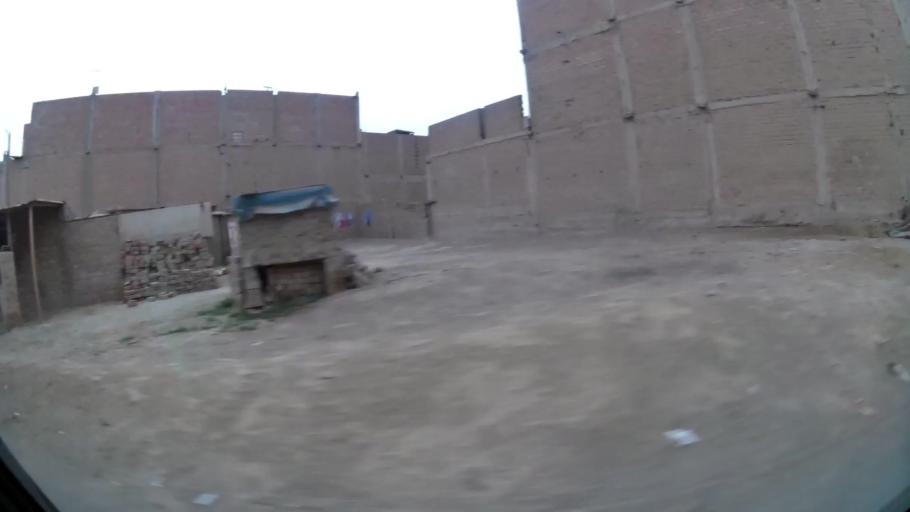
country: PE
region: Lima
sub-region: Lima
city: Independencia
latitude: -11.9805
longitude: -77.0993
